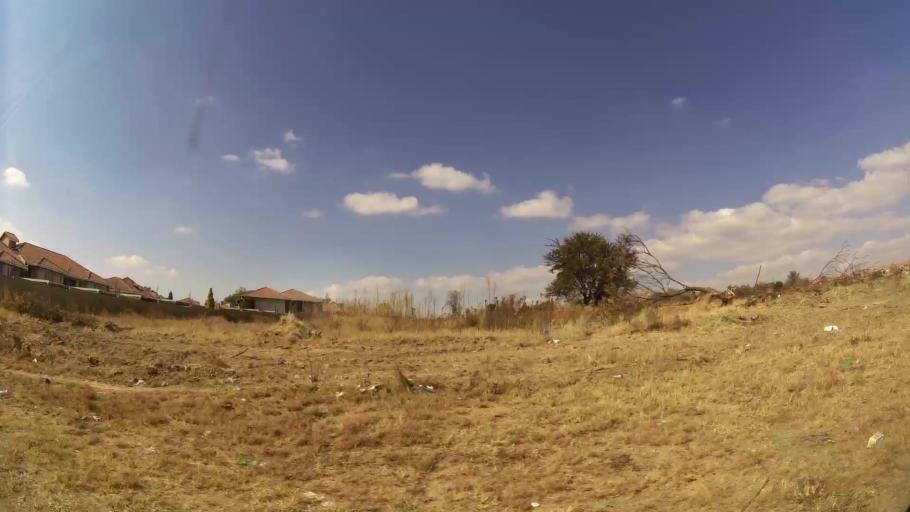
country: ZA
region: Gauteng
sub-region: City of Johannesburg Metropolitan Municipality
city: Midrand
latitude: -26.0062
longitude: 28.1097
